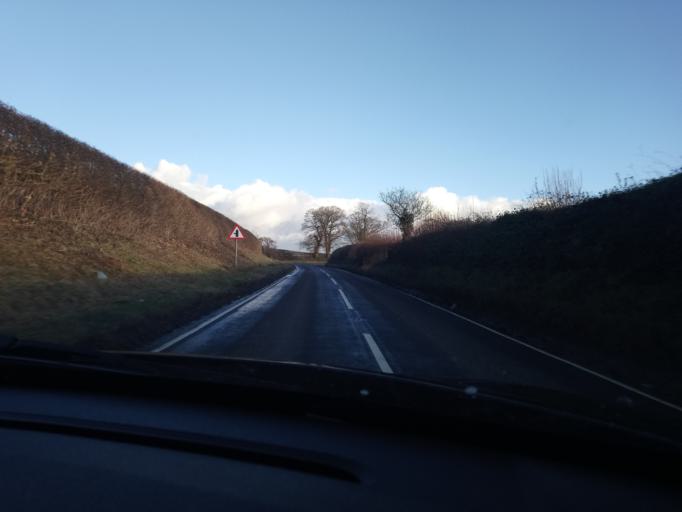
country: GB
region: England
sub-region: Shropshire
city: Wem
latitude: 52.8608
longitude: -2.7519
